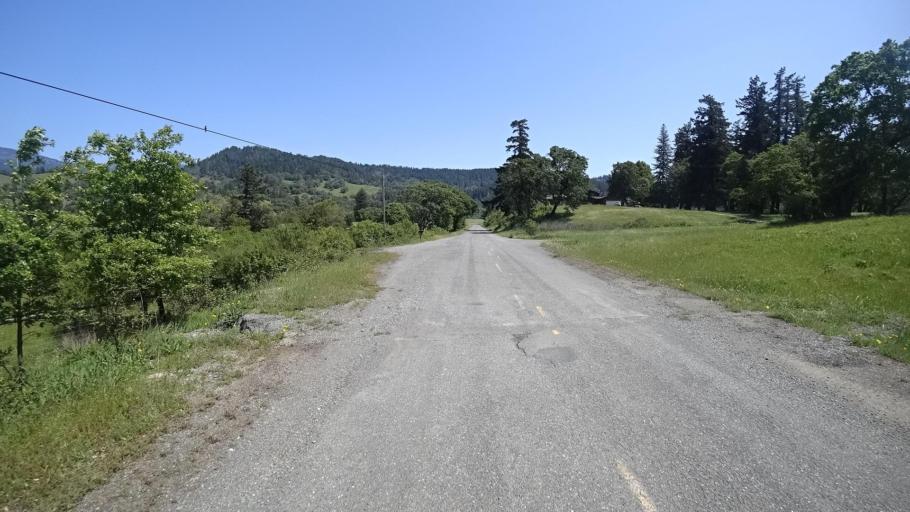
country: US
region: California
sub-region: Humboldt County
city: Redway
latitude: 40.2173
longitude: -123.6429
